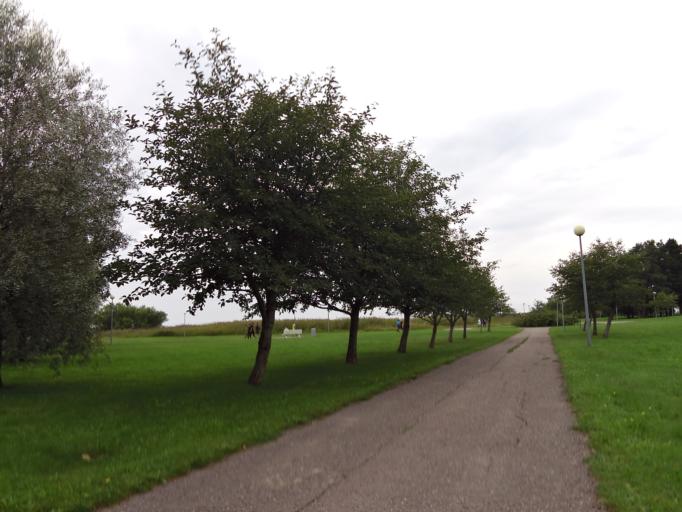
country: EE
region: Harju
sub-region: Tallinna linn
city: Tallinn
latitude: 59.4373
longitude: 24.6835
